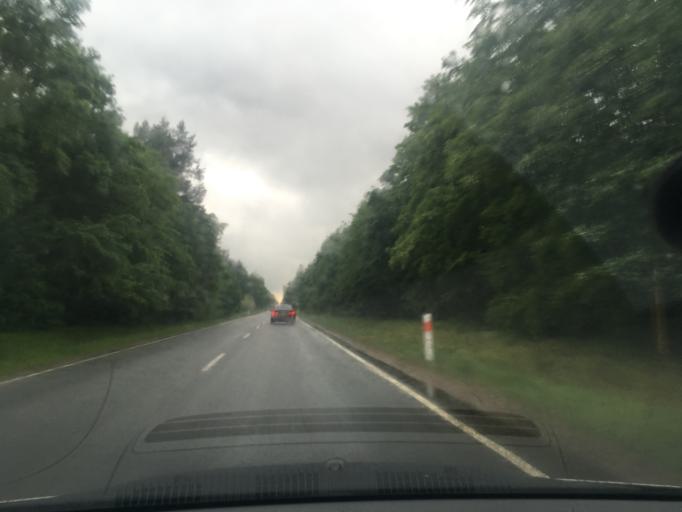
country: PL
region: Lublin Voivodeship
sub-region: Powiat rycki
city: Ryki
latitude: 51.5850
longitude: 21.9260
